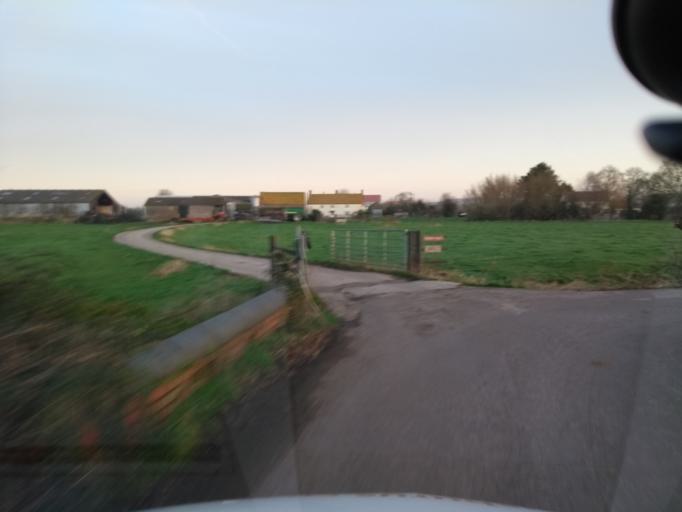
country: GB
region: England
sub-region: Somerset
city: Wedmore
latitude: 51.2294
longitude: -2.8802
